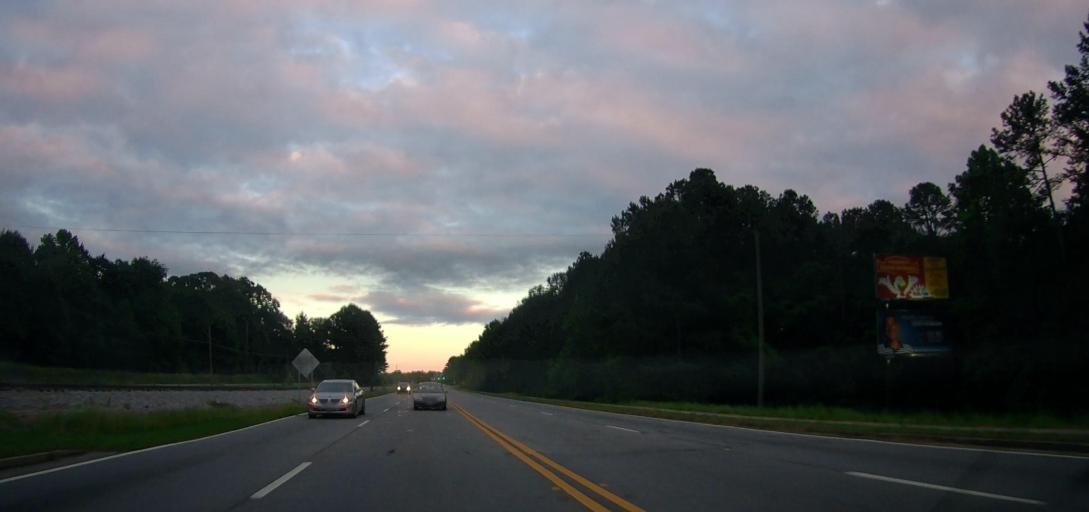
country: US
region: Georgia
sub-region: Clarke County
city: Country Club Estates
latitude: 33.9921
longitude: -83.4338
